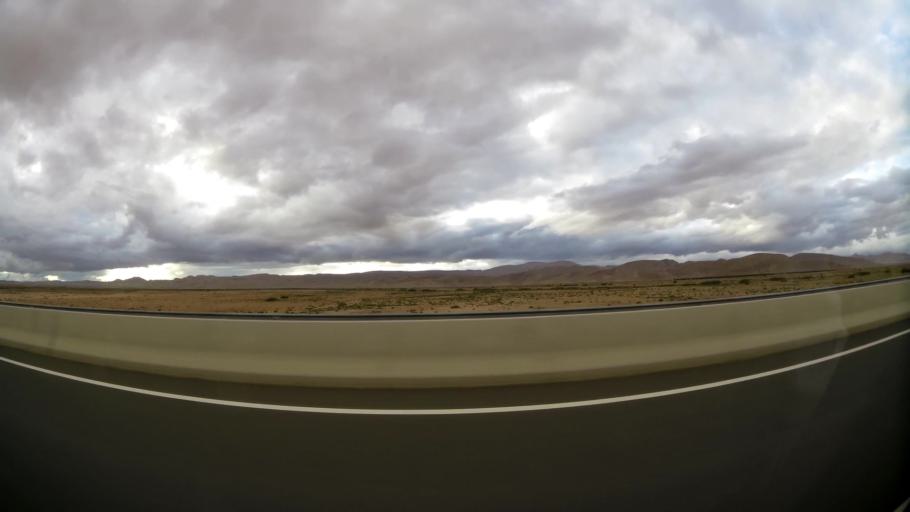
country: MA
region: Taza-Al Hoceima-Taounate
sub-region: Taza
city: Guercif
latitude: 34.3207
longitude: -3.5775
